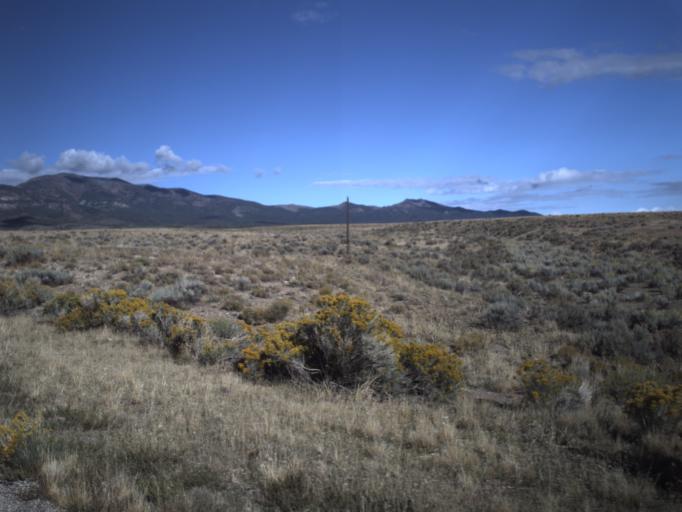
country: US
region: Utah
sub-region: Beaver County
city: Milford
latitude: 38.4452
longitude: -113.1804
